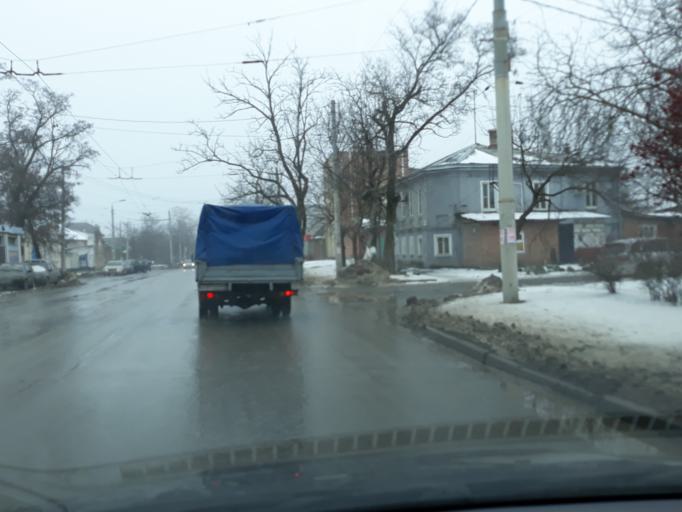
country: RU
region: Rostov
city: Taganrog
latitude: 47.2208
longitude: 38.9069
